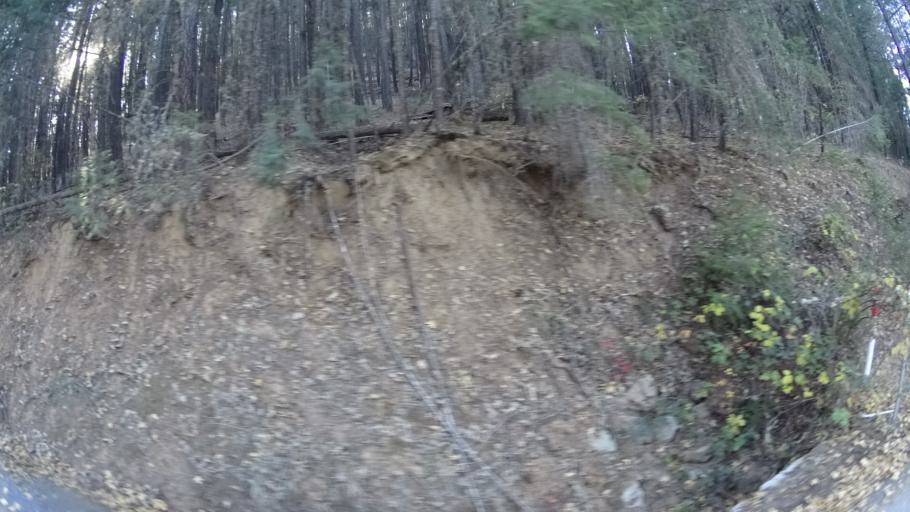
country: US
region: California
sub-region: Siskiyou County
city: Yreka
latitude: 41.8266
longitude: -122.9793
